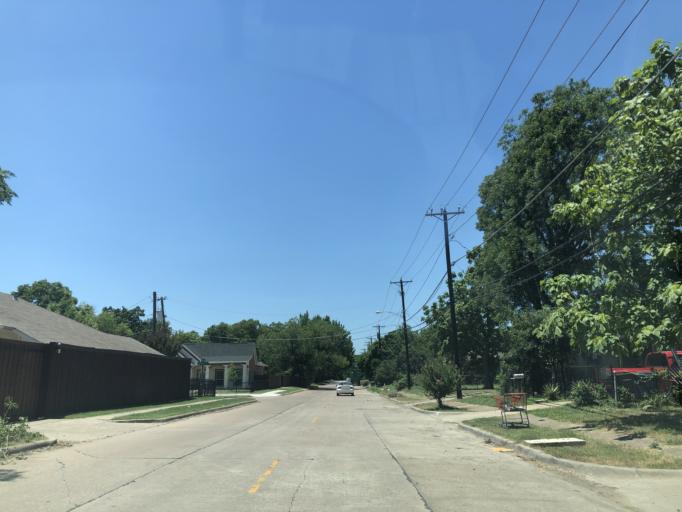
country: US
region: Texas
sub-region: Dallas County
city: Cockrell Hill
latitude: 32.7928
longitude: -96.8882
